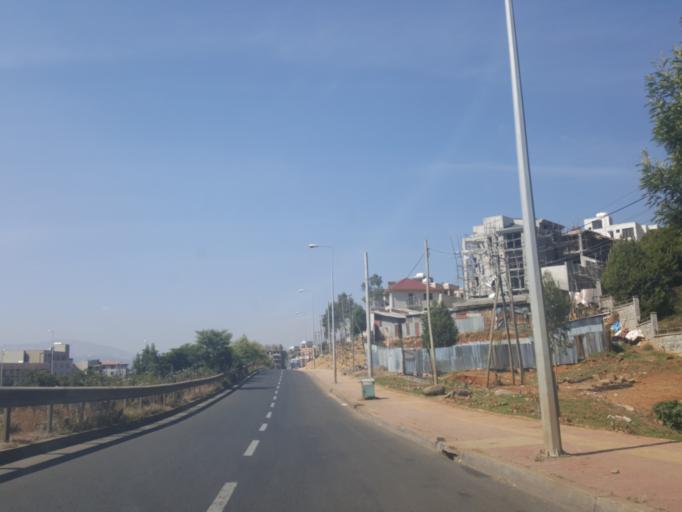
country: ET
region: Adis Abeba
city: Addis Ababa
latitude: 9.0706
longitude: 38.7207
